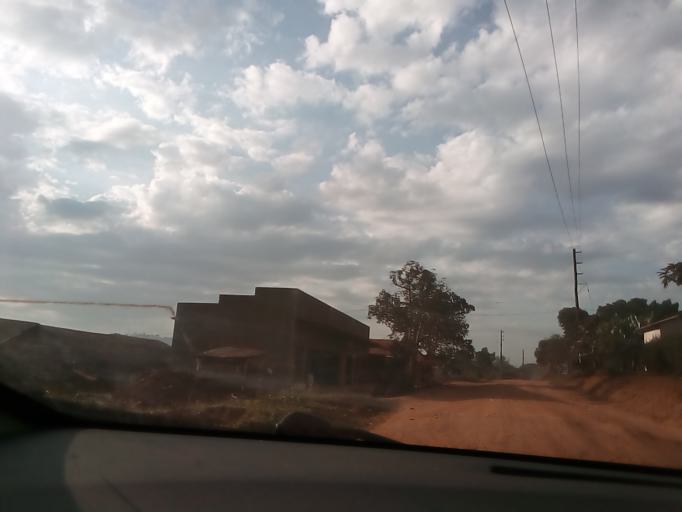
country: UG
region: Central Region
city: Masaka
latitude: -0.3478
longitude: 31.7160
